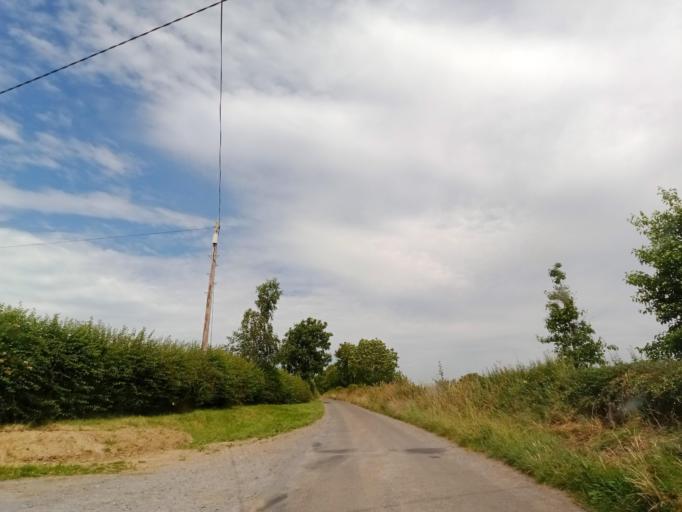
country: IE
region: Leinster
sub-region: Kilkenny
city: Thomastown
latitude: 52.5657
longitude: -7.1254
